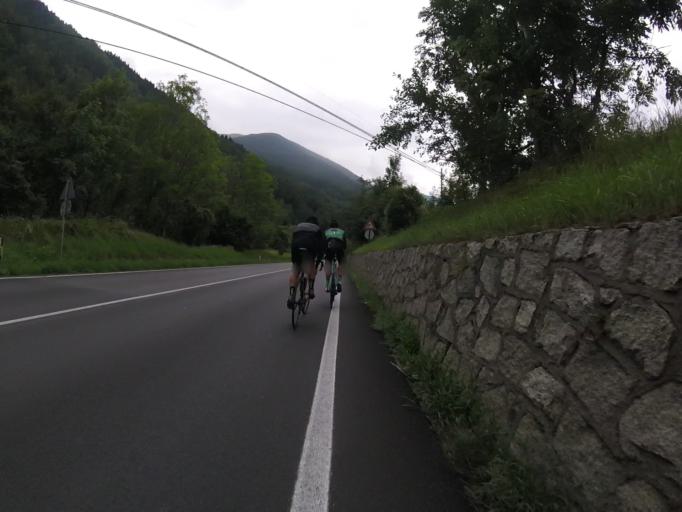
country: IT
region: Lombardy
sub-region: Provincia di Brescia
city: Incudine
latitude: 46.2167
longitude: 10.3528
